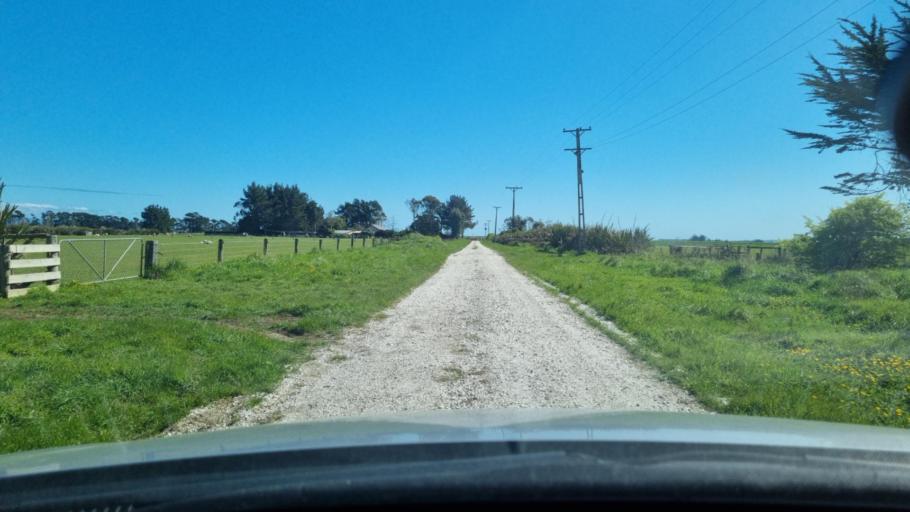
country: NZ
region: Southland
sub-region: Invercargill City
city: Invercargill
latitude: -46.3914
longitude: 168.2955
